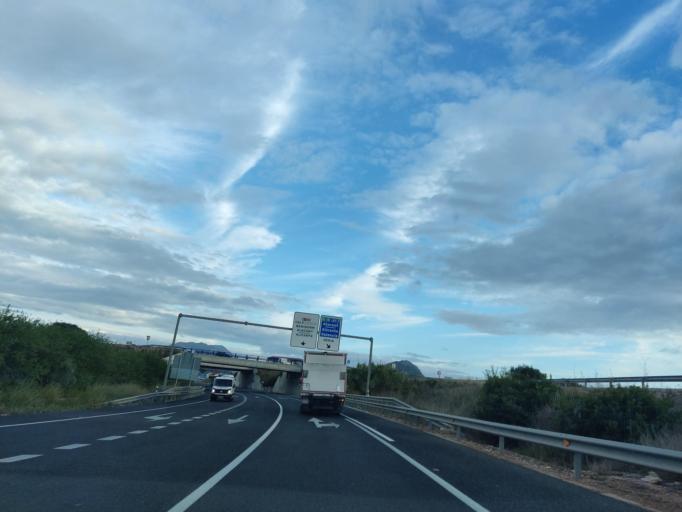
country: ES
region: Valencia
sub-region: Provincia de Alicante
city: Ondara
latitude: 38.8199
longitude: 0.0182
